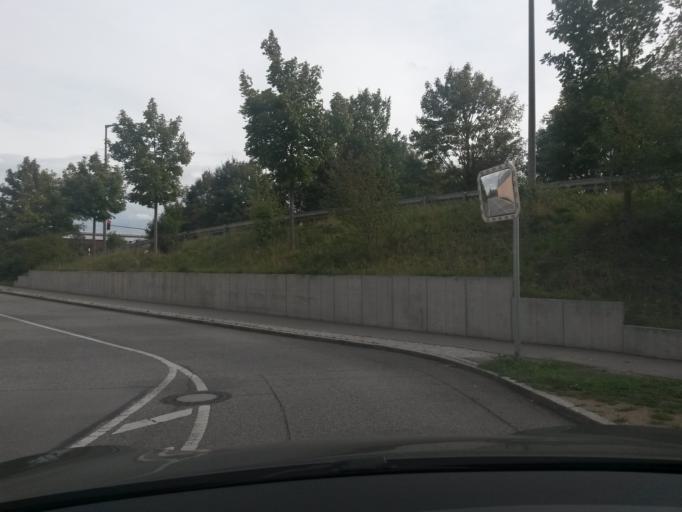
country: DE
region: Bavaria
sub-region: Upper Palatinate
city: Regensburg
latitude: 49.0051
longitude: 12.1412
